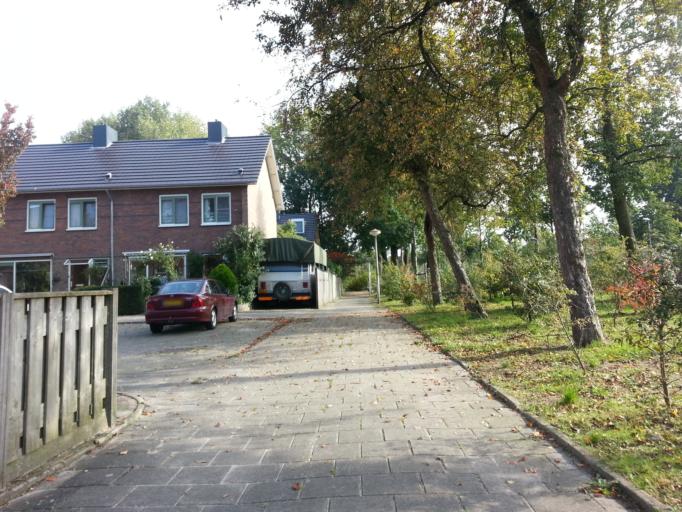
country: NL
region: North Brabant
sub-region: Gemeente Eindhoven
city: Villapark
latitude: 51.4677
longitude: 5.4922
